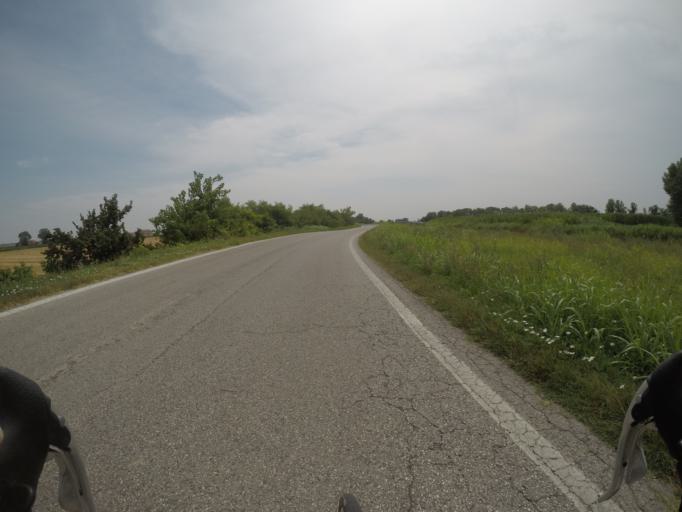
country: IT
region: Veneto
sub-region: Provincia di Rovigo
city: Villanova del Ghebbo Canton
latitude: 45.0530
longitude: 11.6657
